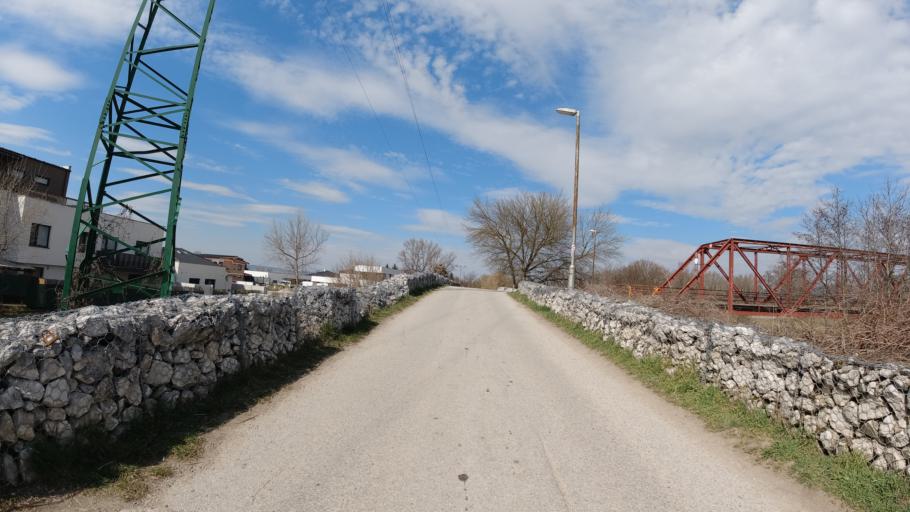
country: SK
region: Trnavsky
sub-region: Okres Trnava
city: Piestany
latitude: 48.6057
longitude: 17.8405
